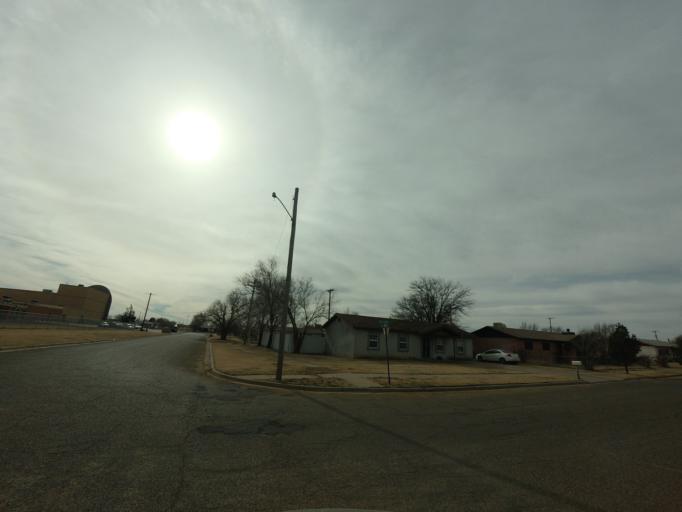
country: US
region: New Mexico
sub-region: Curry County
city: Clovis
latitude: 34.4116
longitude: -103.2425
